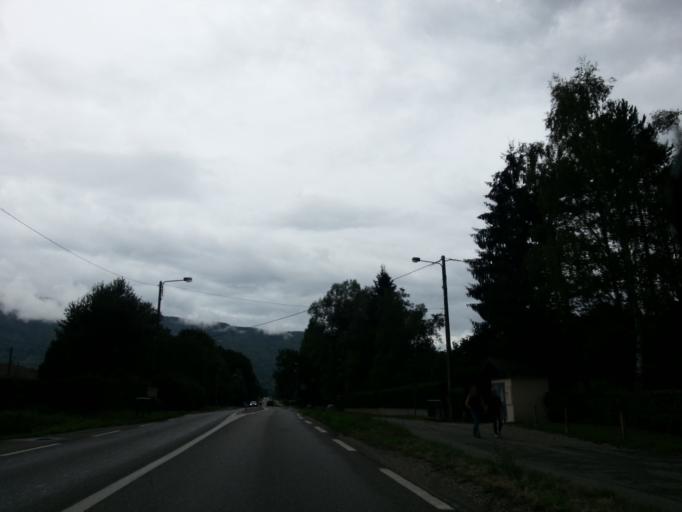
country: FR
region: Rhone-Alpes
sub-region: Departement de la Haute-Savoie
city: Saint-Jorioz
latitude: 45.8288
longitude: 6.1895
